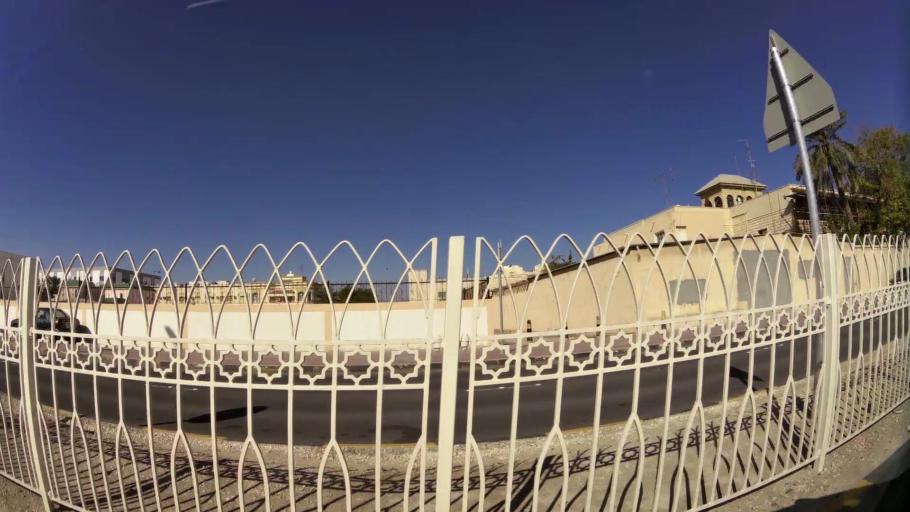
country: BH
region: Muharraq
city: Al Muharraq
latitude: 26.2559
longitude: 50.6080
